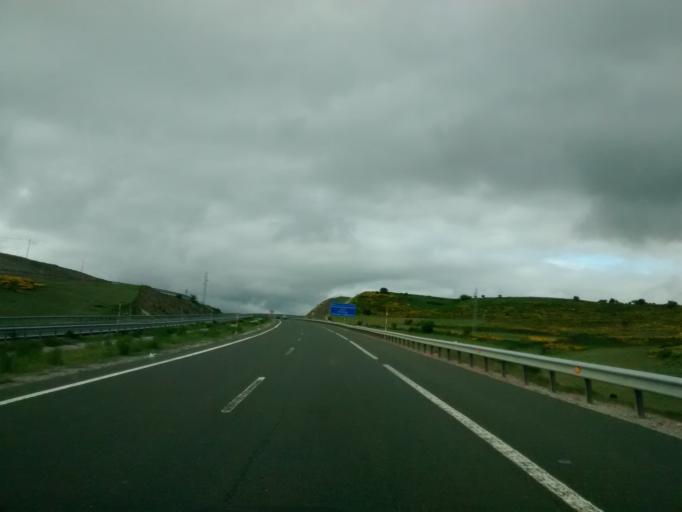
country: ES
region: Cantabria
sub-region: Provincia de Cantabria
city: Mataporquera
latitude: 42.8786
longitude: -4.1395
